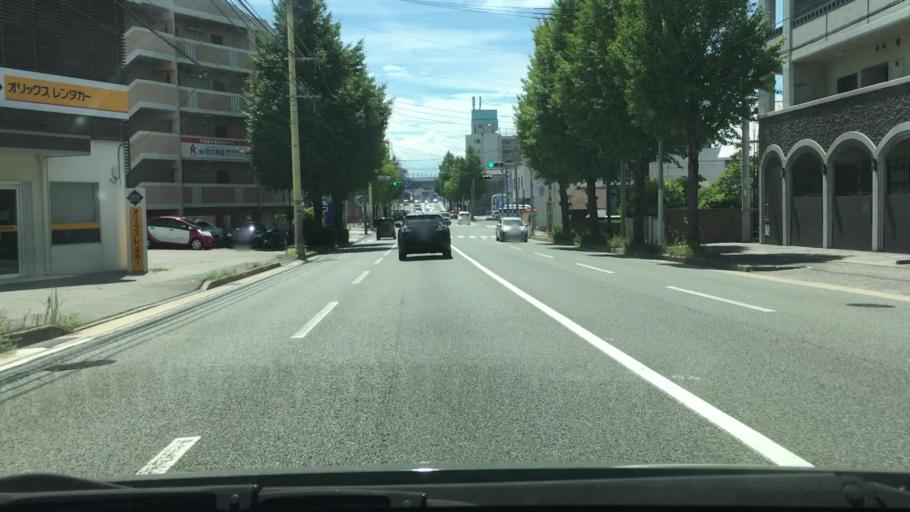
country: JP
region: Fukuoka
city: Onojo
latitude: 33.5581
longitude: 130.4508
